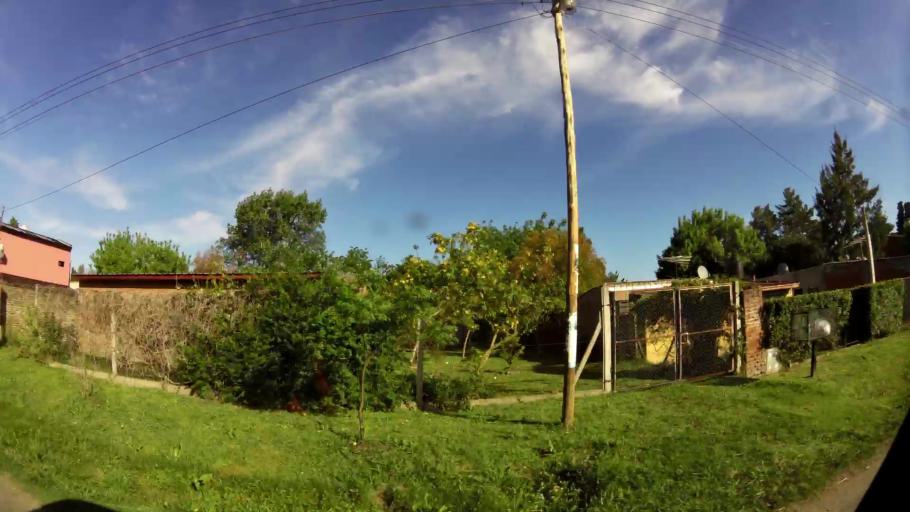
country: AR
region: Buenos Aires
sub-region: Partido de Quilmes
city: Quilmes
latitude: -34.8140
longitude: -58.2144
